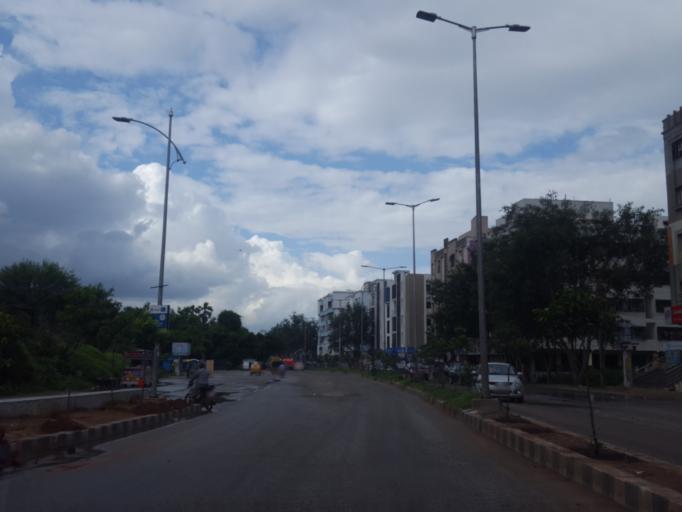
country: IN
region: Telangana
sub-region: Medak
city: Serilingampalle
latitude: 17.4859
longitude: 78.3129
